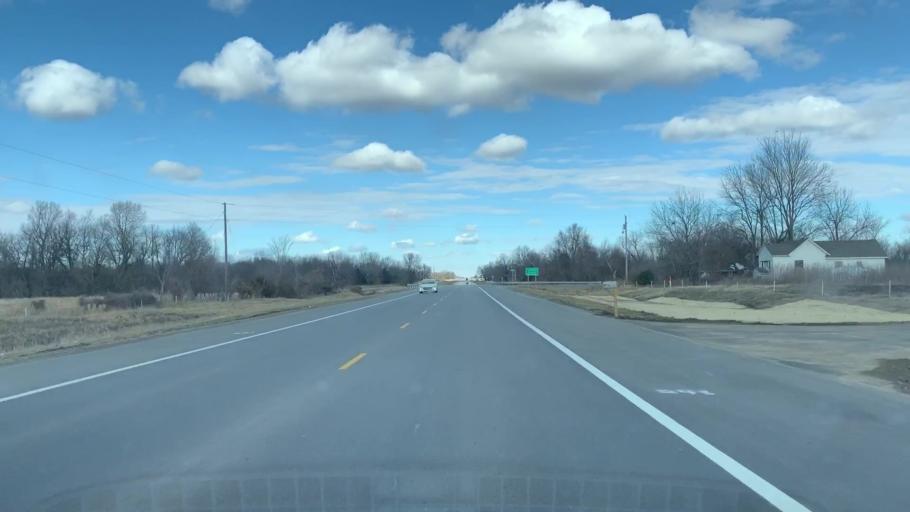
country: US
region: Kansas
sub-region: Cherokee County
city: Columbus
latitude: 37.2728
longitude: -94.8321
